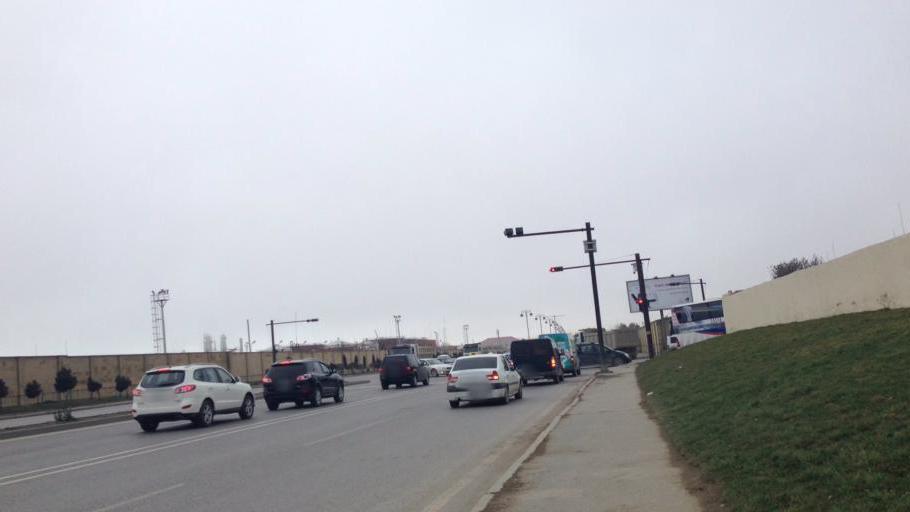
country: AZ
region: Baki
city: Baku
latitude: 40.3766
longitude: 49.9147
